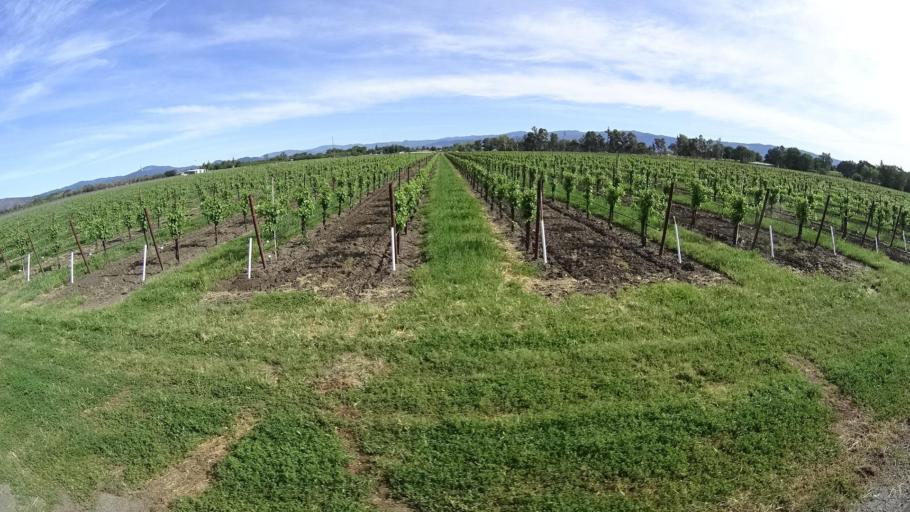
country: US
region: California
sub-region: Lake County
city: Kelseyville
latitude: 38.9825
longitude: -122.8648
